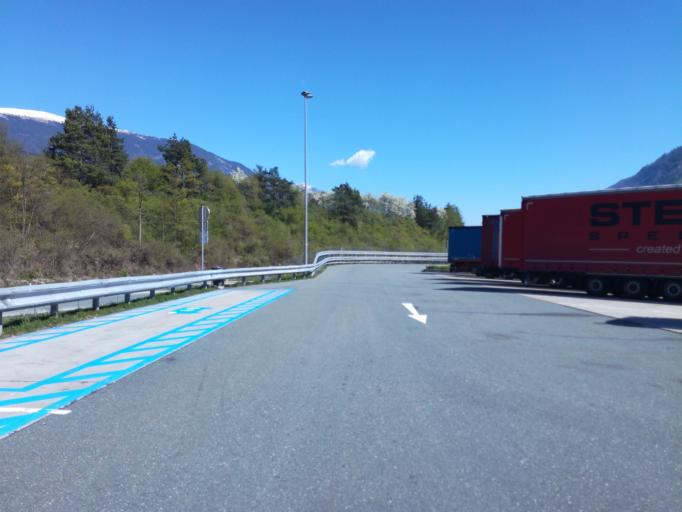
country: AT
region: Tyrol
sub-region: Politischer Bezirk Schwaz
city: Vomp
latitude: 47.3308
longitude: 11.6777
